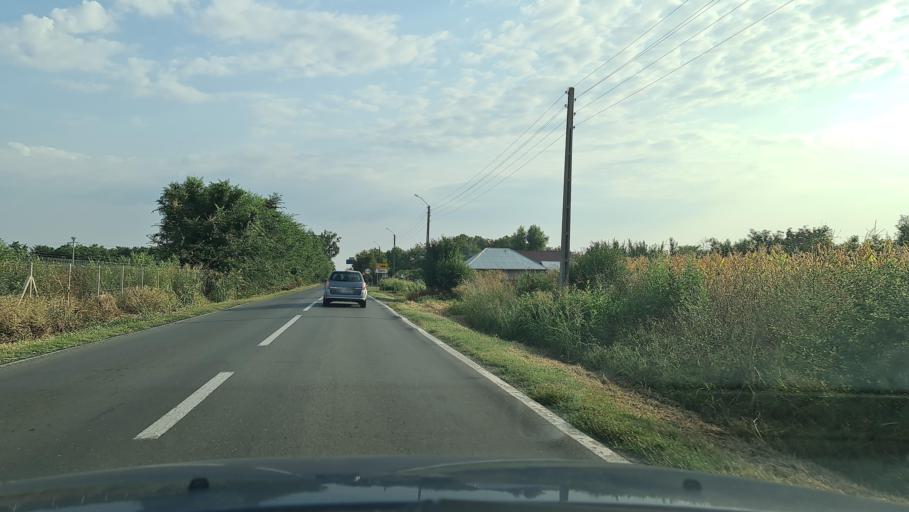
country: RO
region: Calarasi
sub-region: Comuna Dor Marunt
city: Dor Marunt
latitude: 44.4531
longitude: 26.8995
